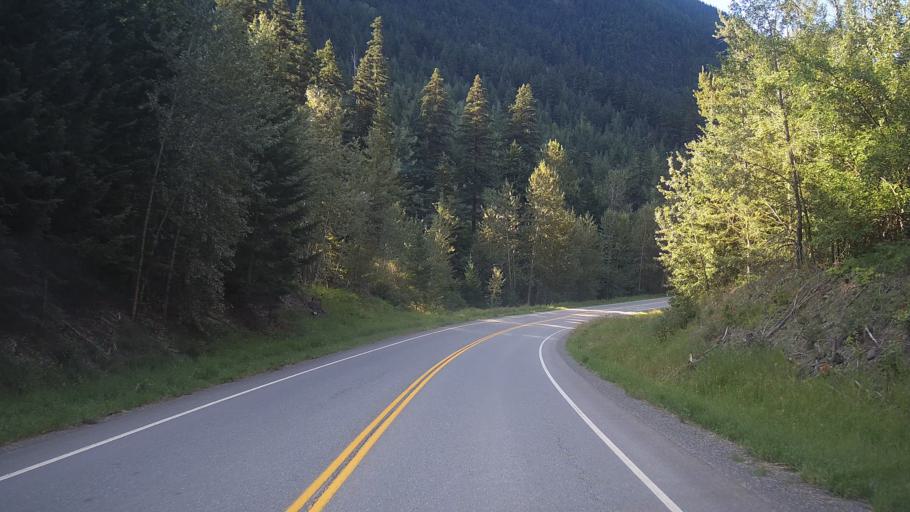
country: CA
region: British Columbia
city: Lillooet
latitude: 50.5625
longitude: -122.0911
